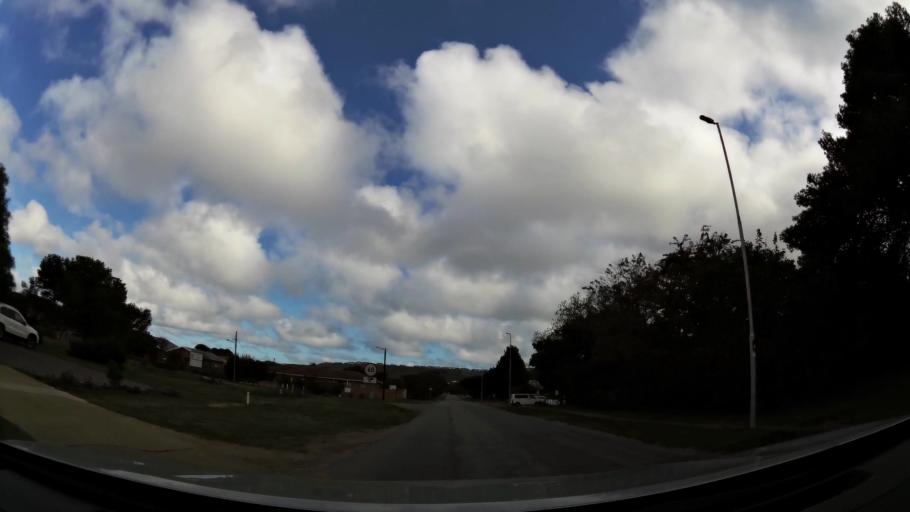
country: ZA
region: Western Cape
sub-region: Eden District Municipality
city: Plettenberg Bay
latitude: -34.0751
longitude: 23.3661
